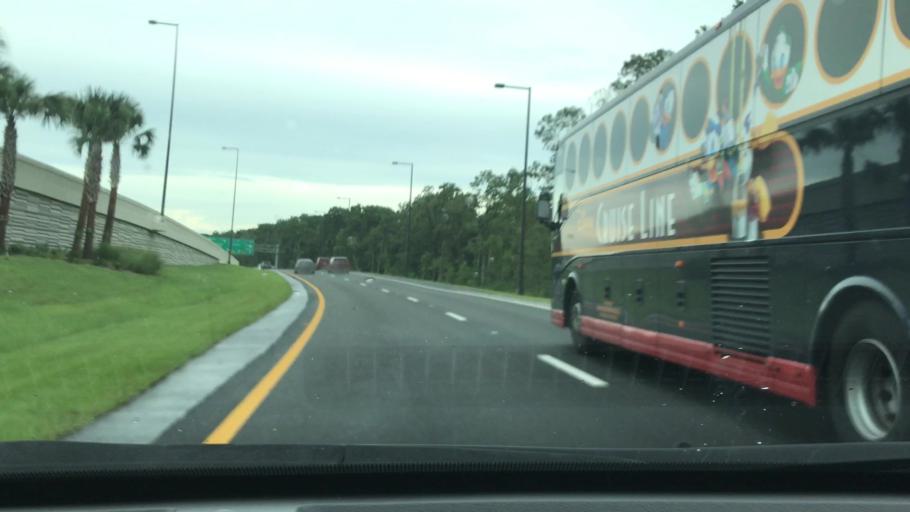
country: US
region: Florida
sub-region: Osceola County
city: Celebration
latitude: 28.3684
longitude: -81.5375
